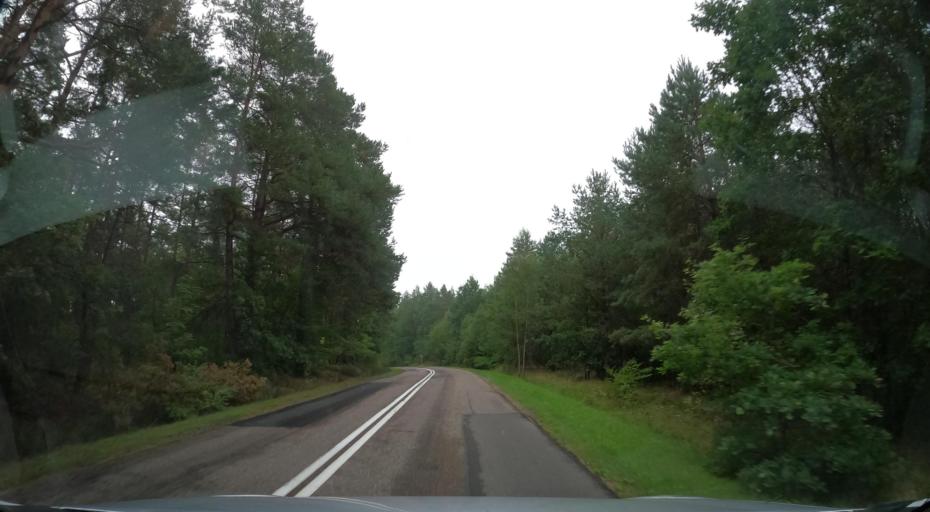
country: PL
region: Pomeranian Voivodeship
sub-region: Powiat wejherowski
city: Linia
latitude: 54.4659
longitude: 17.9917
